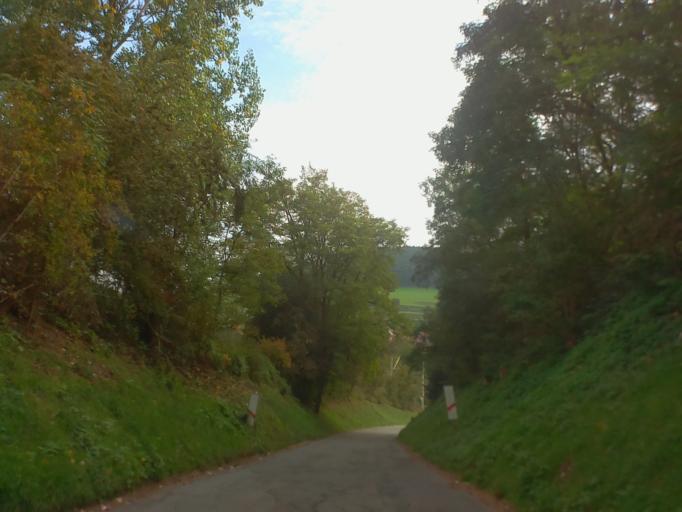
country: DE
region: Thuringia
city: Grosspurschutz
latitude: 50.8230
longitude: 11.5870
